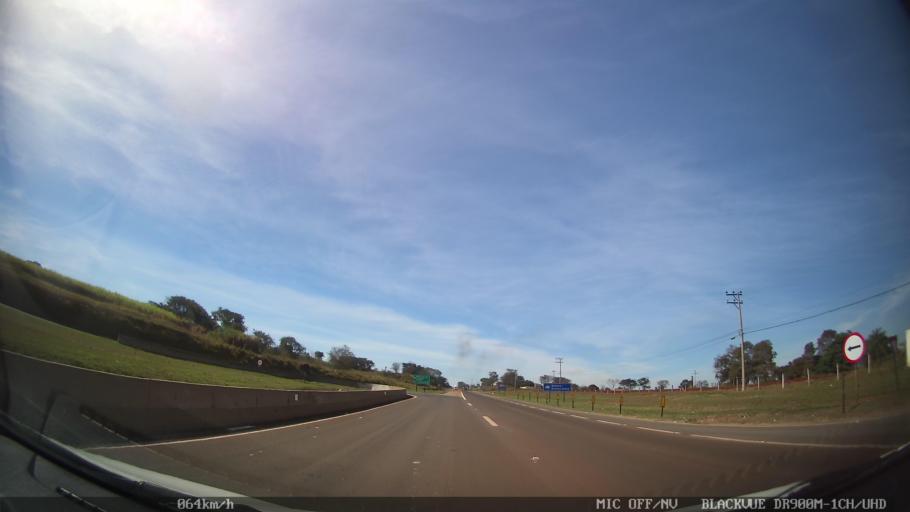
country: BR
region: Sao Paulo
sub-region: Porto Ferreira
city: Porto Ferreira
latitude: -21.8354
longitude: -47.4918
